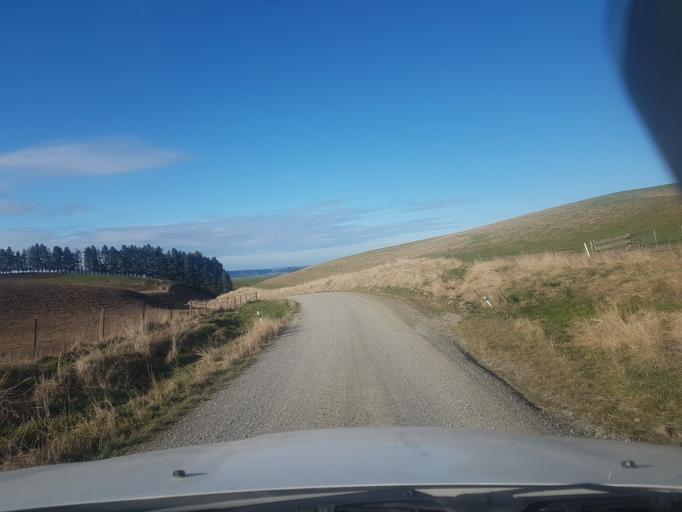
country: NZ
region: Canterbury
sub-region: Timaru District
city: Pleasant Point
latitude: -44.1665
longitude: 170.8941
